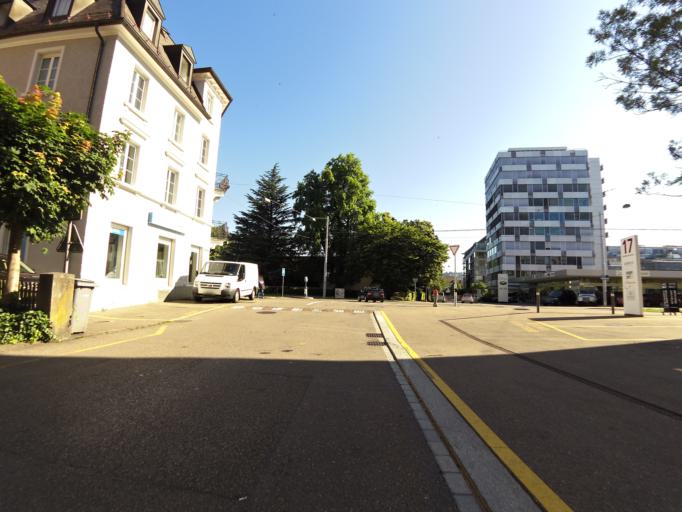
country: CH
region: Zurich
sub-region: Bezirk Zuerich
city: Zuerich (Kreis 9) / Altstetten
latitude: 47.3856
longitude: 8.4928
